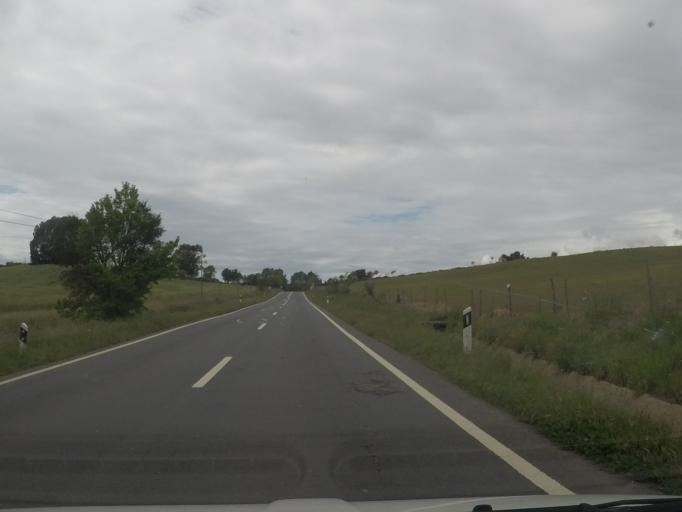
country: PT
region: Setubal
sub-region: Santiago do Cacem
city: Cercal
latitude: 37.8248
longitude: -8.6936
